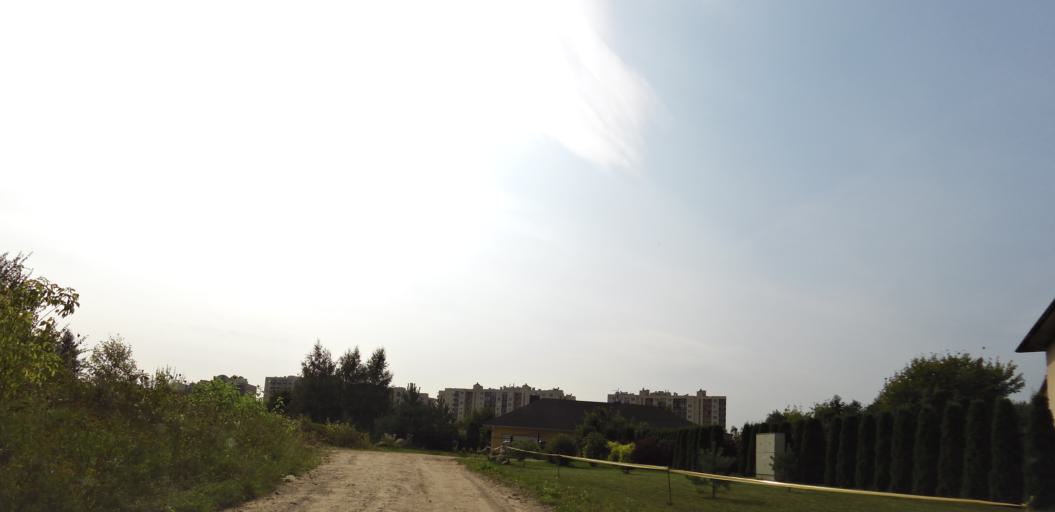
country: LT
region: Vilnius County
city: Pasilaiciai
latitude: 54.7456
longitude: 25.2303
